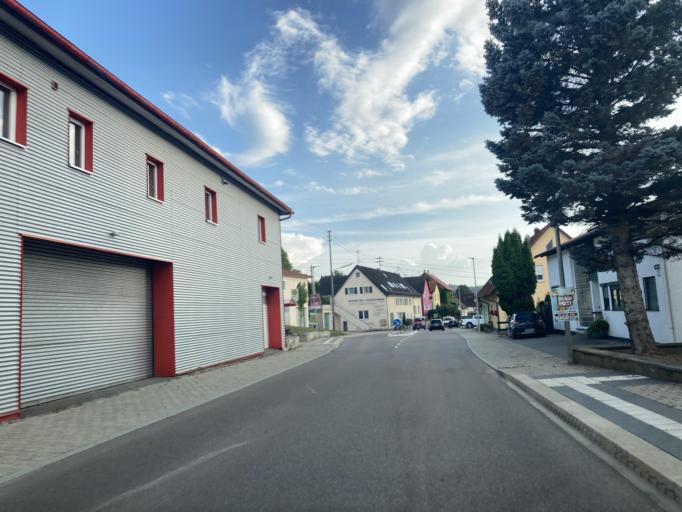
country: DE
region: Baden-Wuerttemberg
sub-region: Regierungsbezirk Stuttgart
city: Dischingen
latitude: 48.6988
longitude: 10.3661
